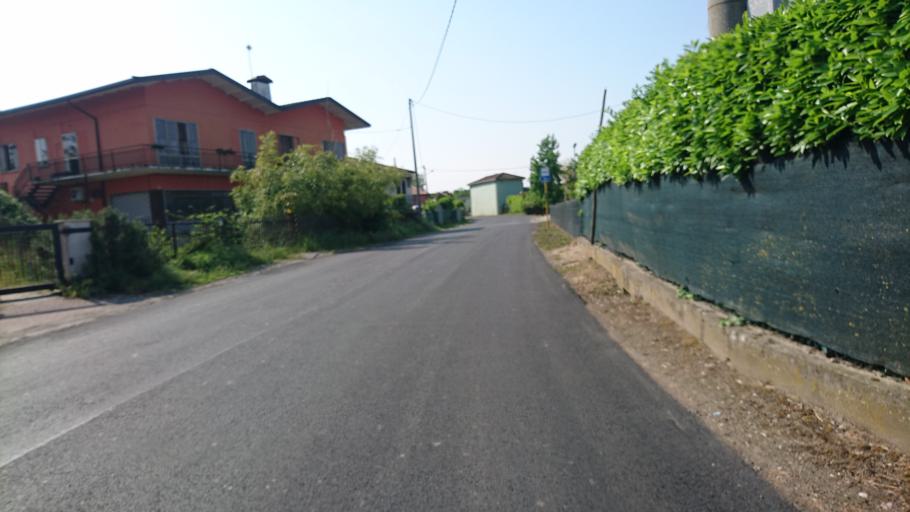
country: IT
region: Veneto
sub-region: Provincia di Padova
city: Saonara
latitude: 45.3734
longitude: 11.9955
